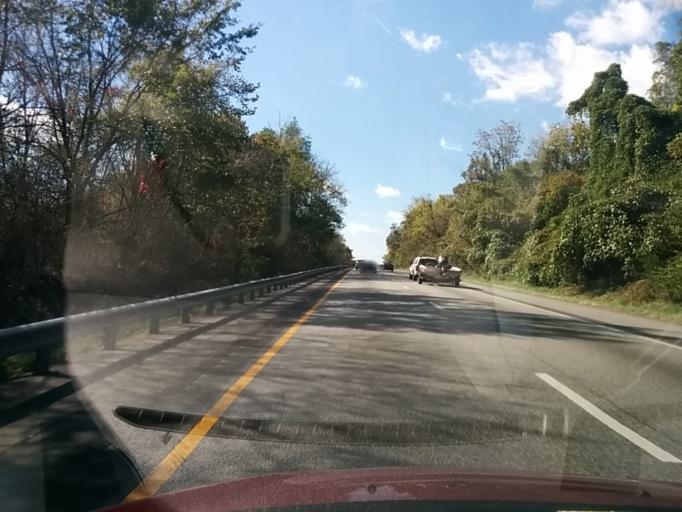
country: US
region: Virginia
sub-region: Botetourt County
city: Daleville
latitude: 37.4239
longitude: -79.8799
